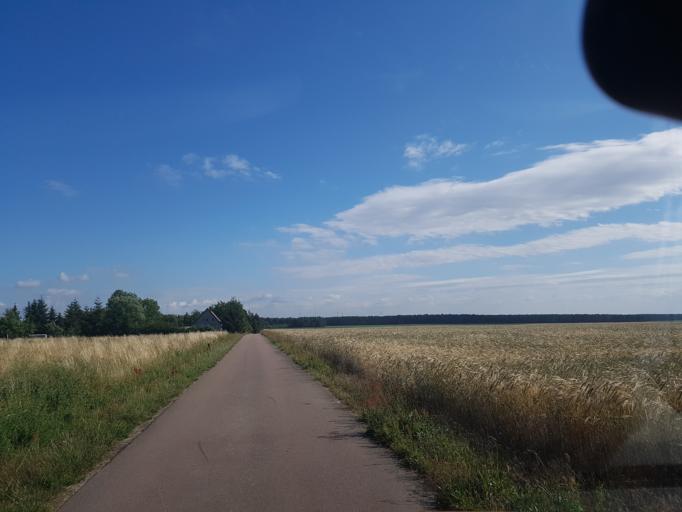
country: DE
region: Brandenburg
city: Juterbog
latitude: 51.9029
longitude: 13.1380
